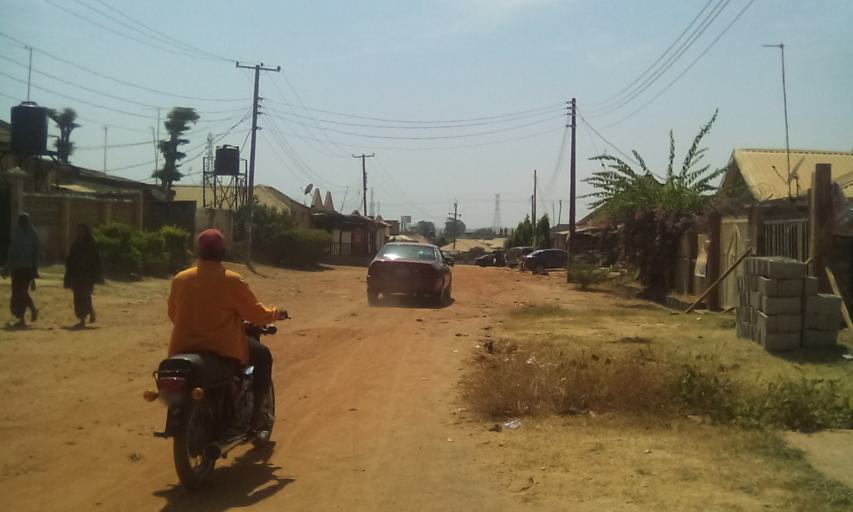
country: NG
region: Abuja Federal Capital Territory
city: Abuja
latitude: 8.9851
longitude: 7.3710
